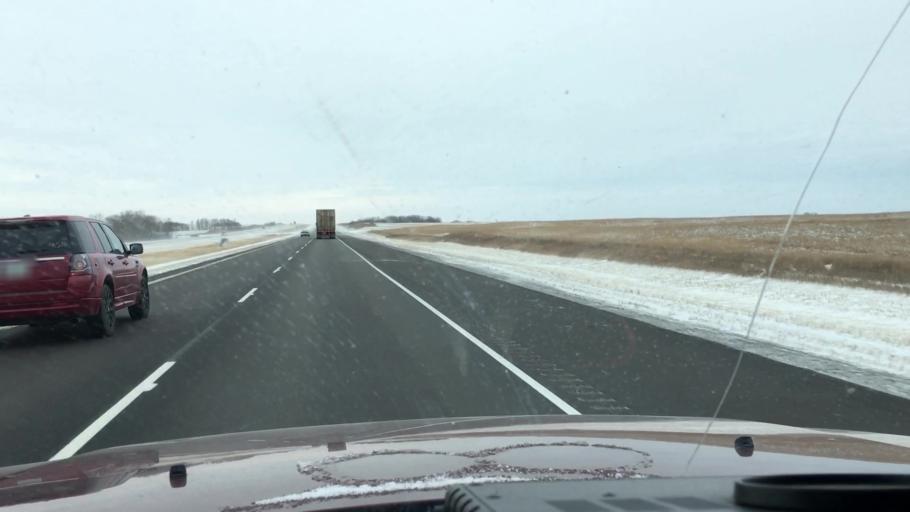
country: CA
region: Saskatchewan
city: Saskatoon
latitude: 51.6819
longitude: -106.4537
